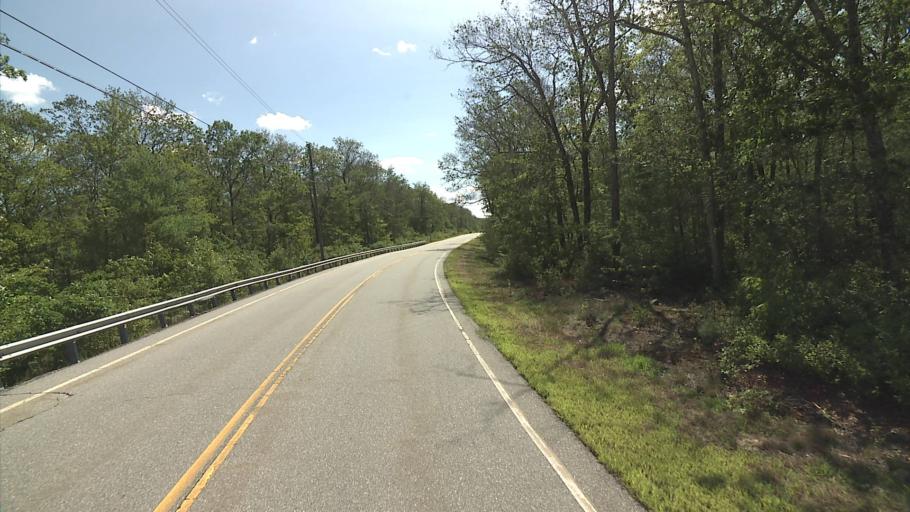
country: US
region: Rhode Island
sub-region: Washington County
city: Hope Valley
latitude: 41.5581
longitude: -71.7969
